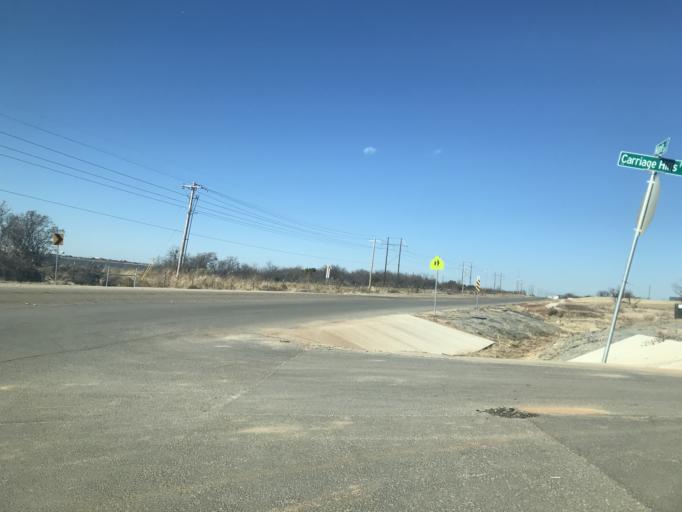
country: US
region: Texas
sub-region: Taylor County
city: Potosi
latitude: 32.3682
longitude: -99.7252
